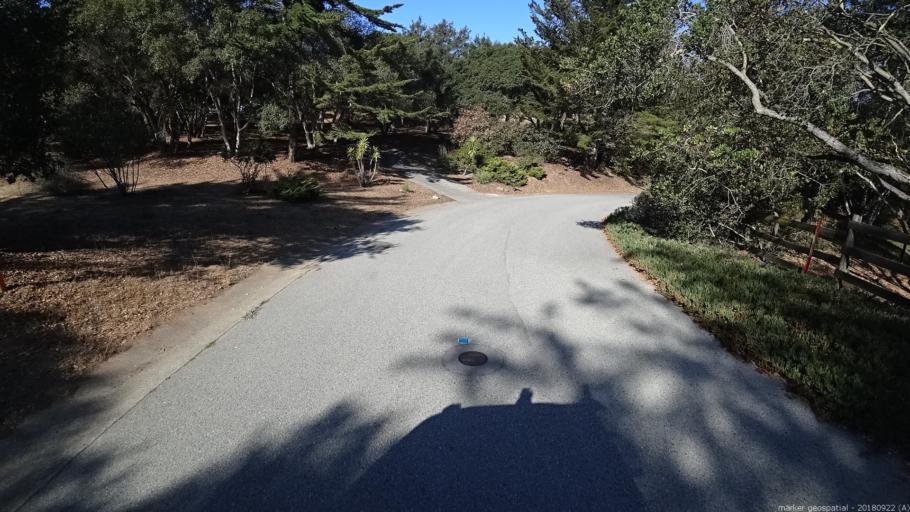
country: US
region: California
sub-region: Monterey County
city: Prunedale
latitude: 36.8254
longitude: -121.6391
